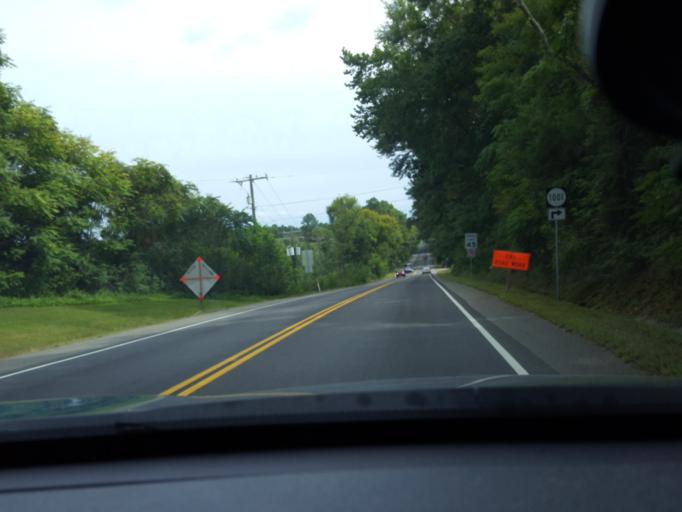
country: US
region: Virginia
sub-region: Hanover County
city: Hanover
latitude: 37.7618
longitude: -77.3666
